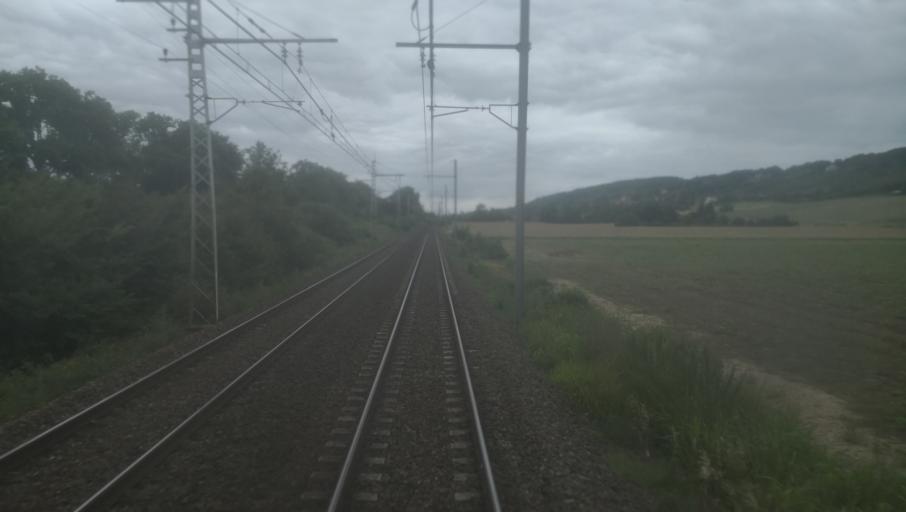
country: FR
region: Midi-Pyrenees
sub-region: Departement de la Haute-Garonne
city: Castelnau-d'Estretefonds
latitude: 43.7936
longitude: 1.3344
